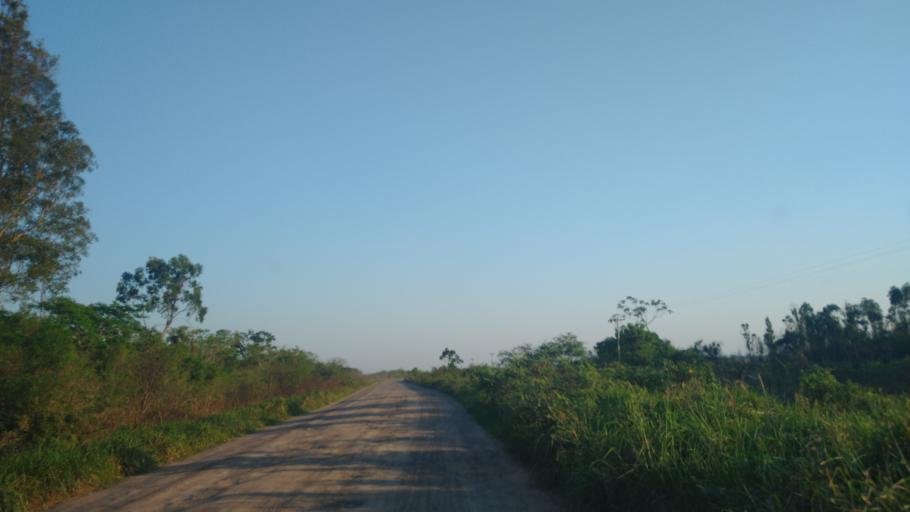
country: PY
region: Neembucu
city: Cerrito
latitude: -27.3958
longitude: -57.6584
